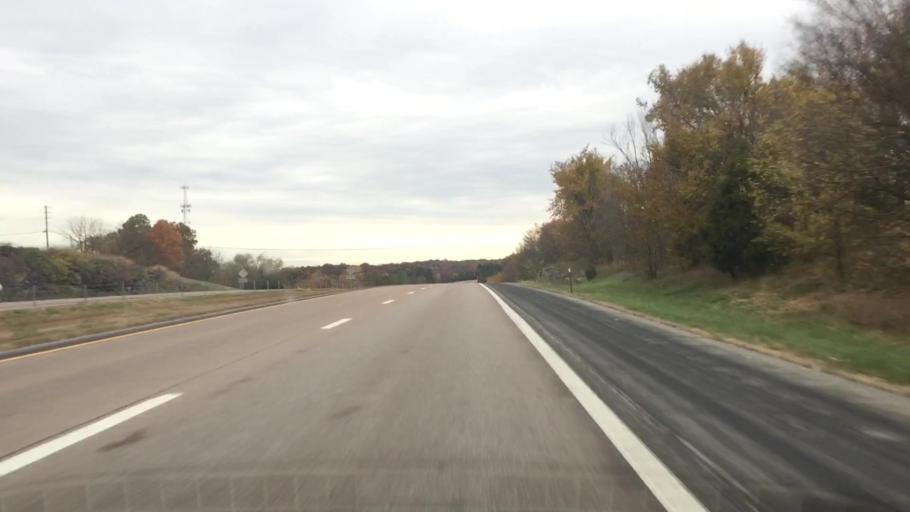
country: US
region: Missouri
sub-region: Boone County
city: Ashland
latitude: 38.6737
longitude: -92.2402
